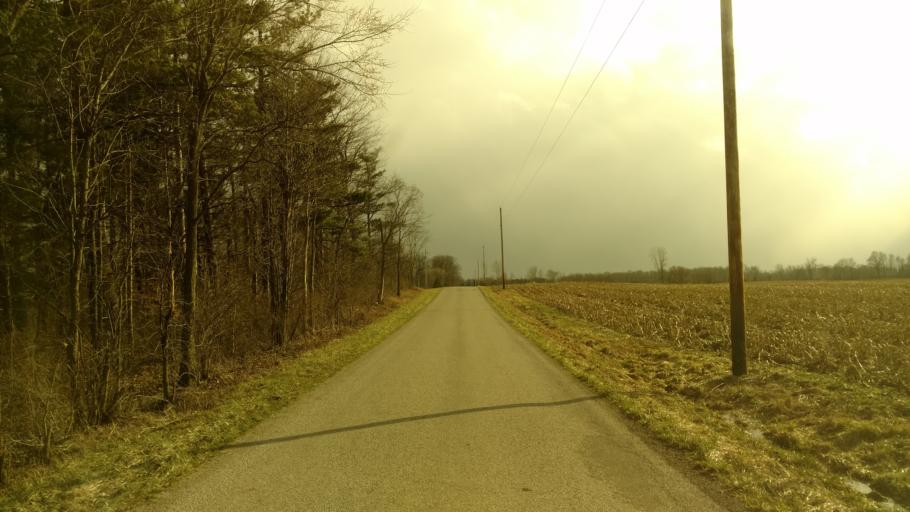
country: US
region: Ohio
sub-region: Crawford County
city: Galion
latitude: 40.7014
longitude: -82.7319
